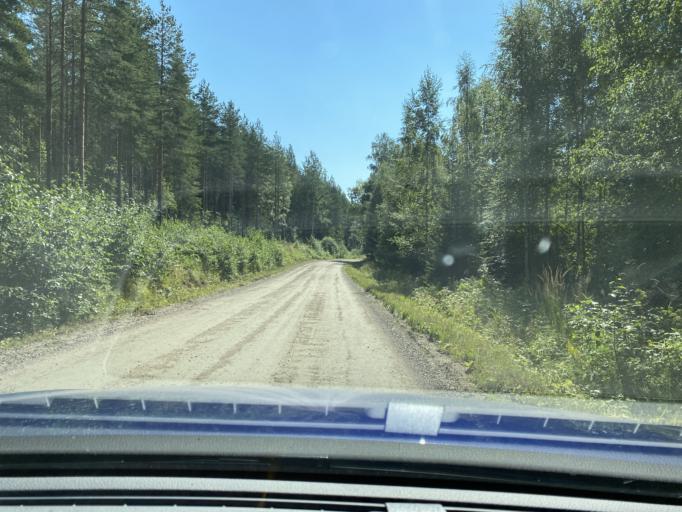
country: FI
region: Central Finland
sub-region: Jyvaeskylae
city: Korpilahti
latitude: 61.8712
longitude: 25.4189
